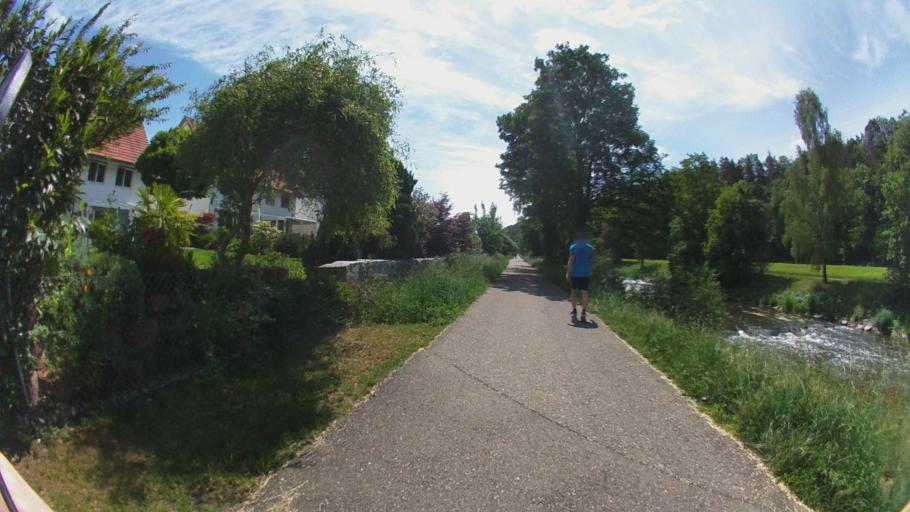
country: CH
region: Zurich
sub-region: Bezirk Buelach
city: Glattfelden
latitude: 47.5554
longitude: 8.4994
